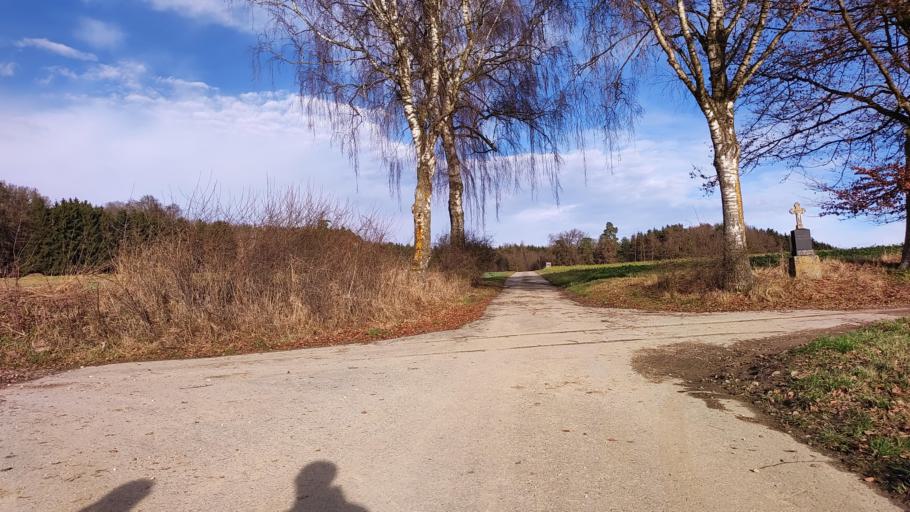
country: DE
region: Bavaria
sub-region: Swabia
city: Zusmarshausen
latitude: 48.3908
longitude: 10.5711
